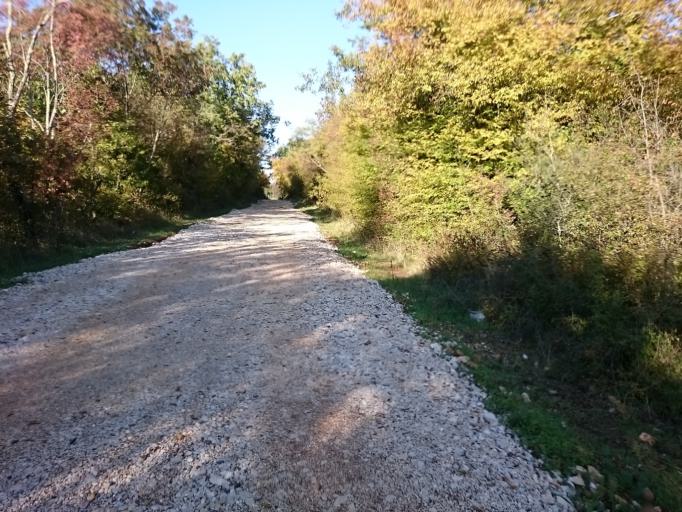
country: HR
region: Istarska
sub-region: Grad Porec
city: Porec
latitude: 45.2475
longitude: 13.6233
